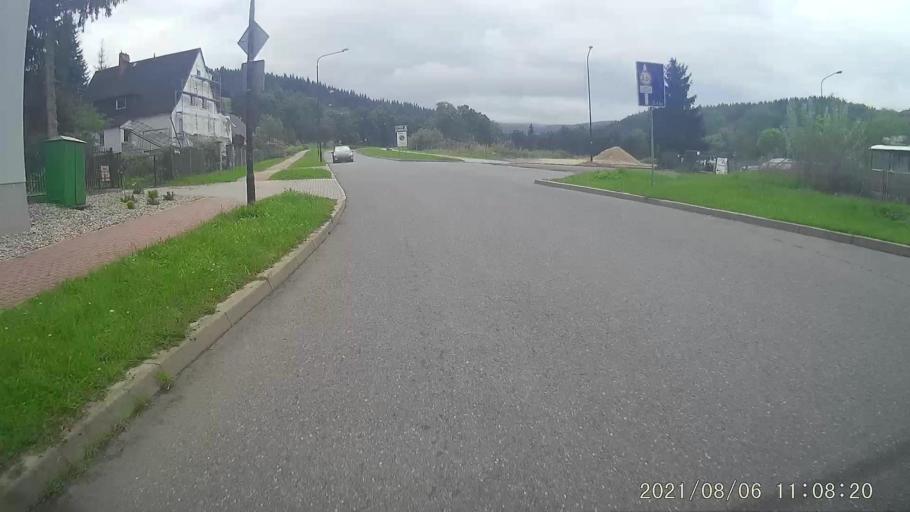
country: PL
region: Lower Silesian Voivodeship
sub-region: Powiat klodzki
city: Duszniki-Zdroj
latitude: 50.4000
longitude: 16.3923
